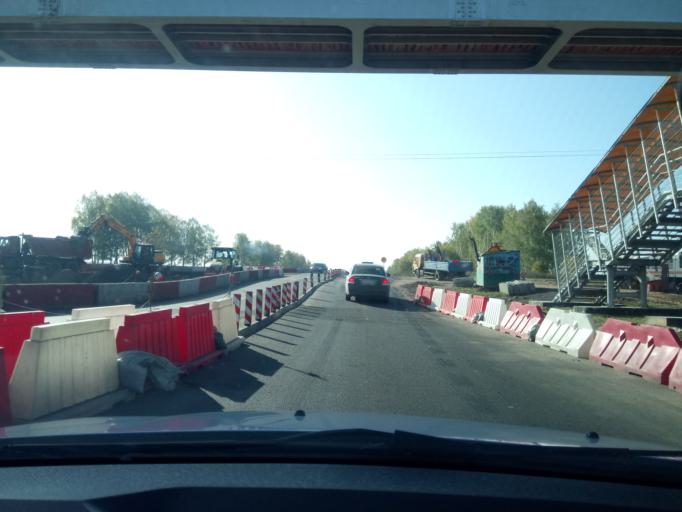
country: RU
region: Nizjnij Novgorod
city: Dal'neye Konstantinovo
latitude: 55.9998
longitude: 43.9679
